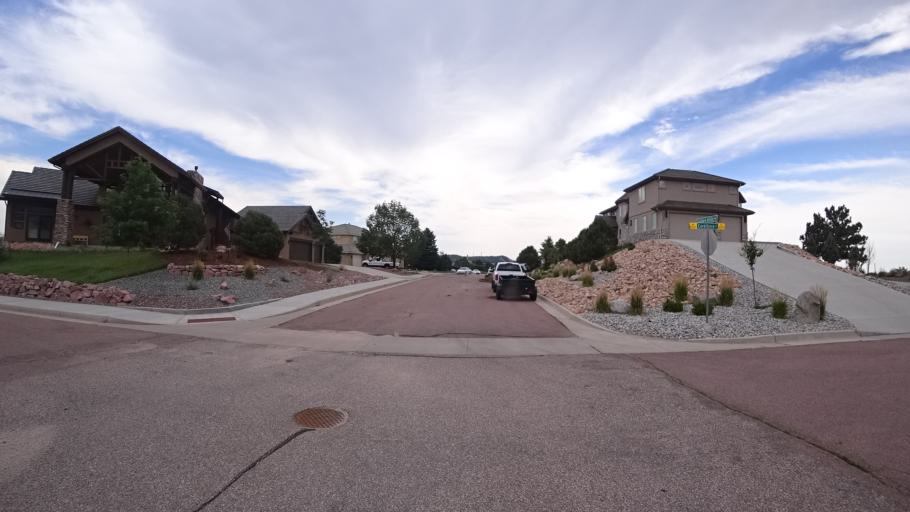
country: US
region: Colorado
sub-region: El Paso County
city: Colorado Springs
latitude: 38.9087
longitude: -104.8331
